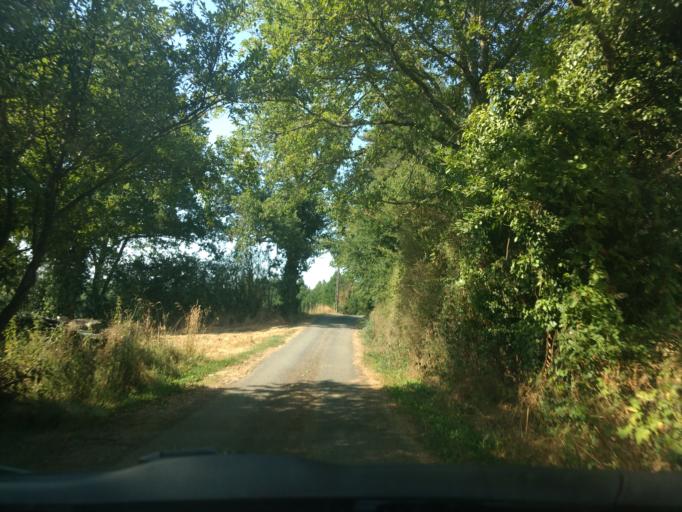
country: FR
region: Midi-Pyrenees
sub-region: Departement de l'Aveyron
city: Livinhac-le-Haut
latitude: 44.6095
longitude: 2.1590
